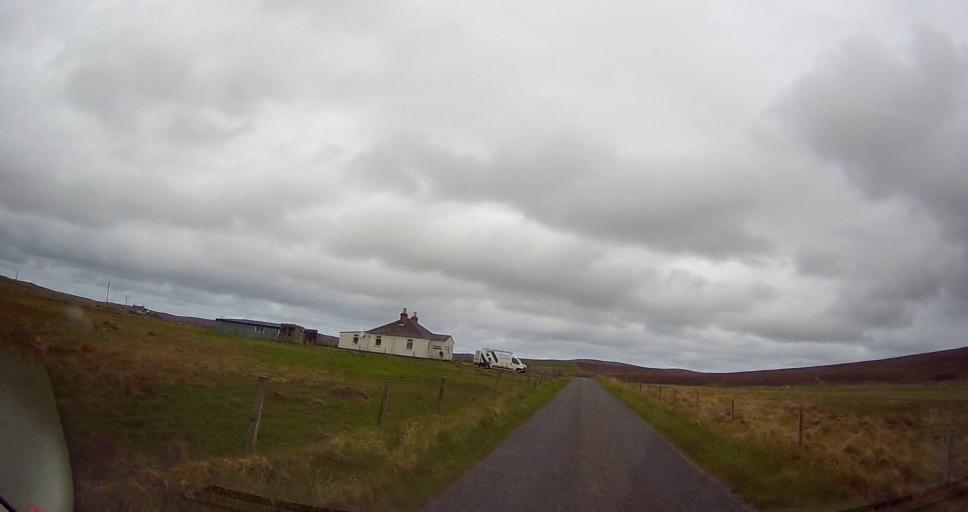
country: GB
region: Scotland
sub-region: Shetland Islands
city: Shetland
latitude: 60.7907
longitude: -0.8452
